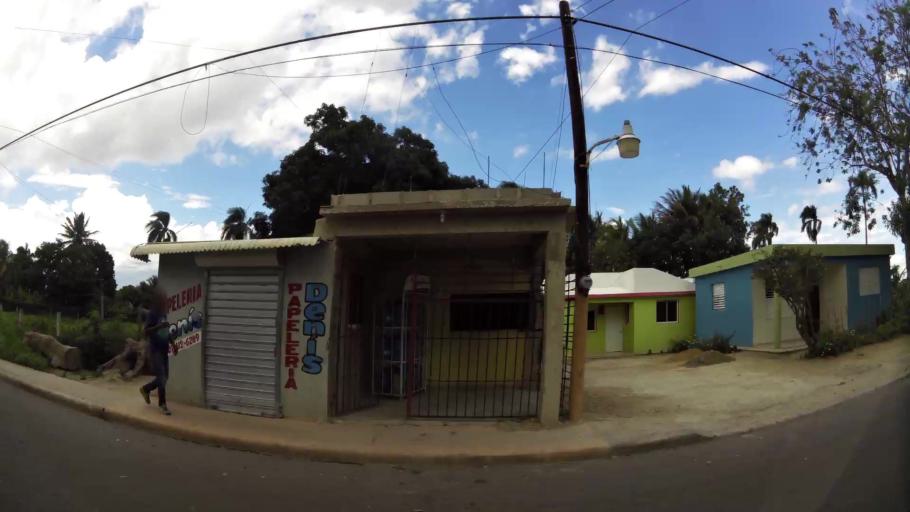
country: DO
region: Santiago
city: Licey al Medio
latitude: 19.3940
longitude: -70.6444
